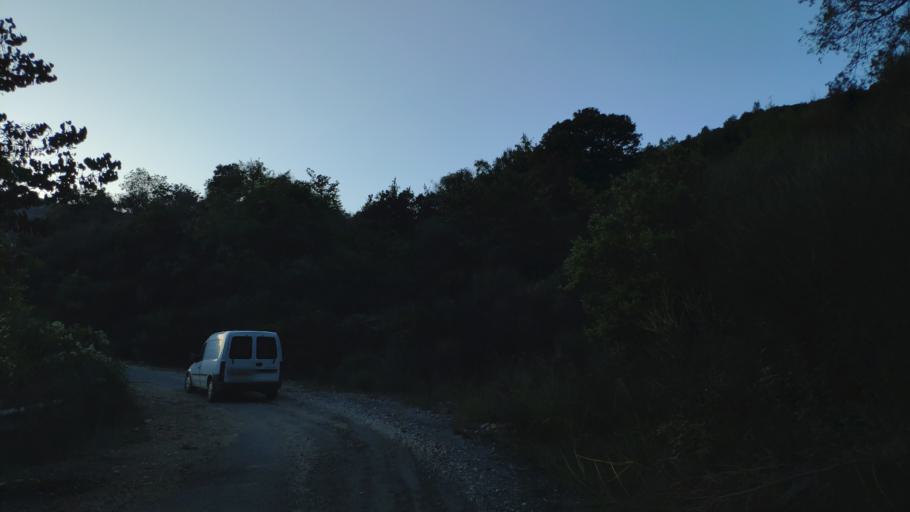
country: GR
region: Peloponnese
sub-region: Nomos Arkadias
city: Dimitsana
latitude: 37.5759
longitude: 22.0526
